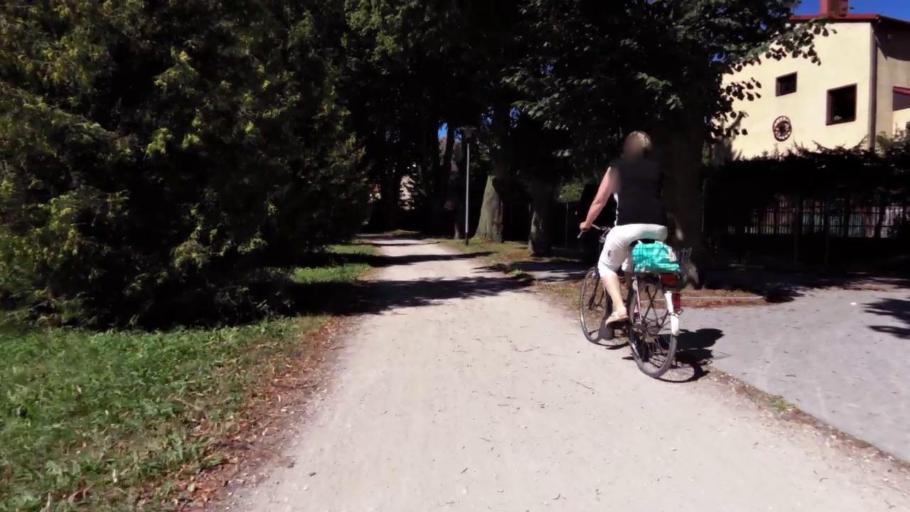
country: PL
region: West Pomeranian Voivodeship
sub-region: Powiat szczecinecki
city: Szczecinek
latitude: 53.7136
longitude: 16.6750
